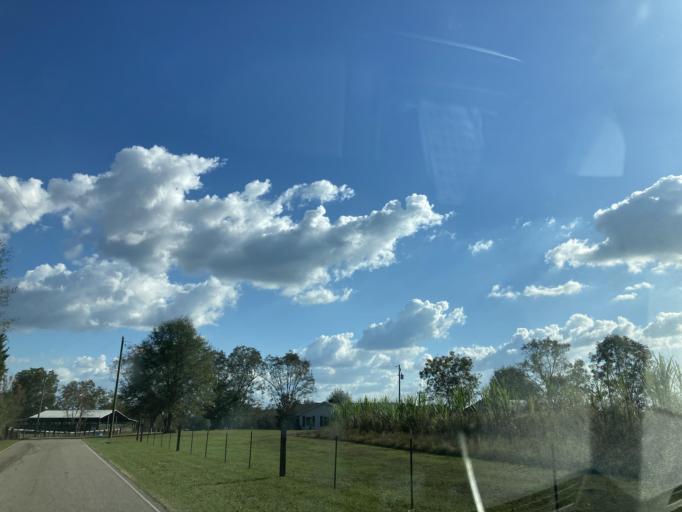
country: US
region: Mississippi
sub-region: Lamar County
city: Sumrall
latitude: 31.4200
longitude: -89.6252
